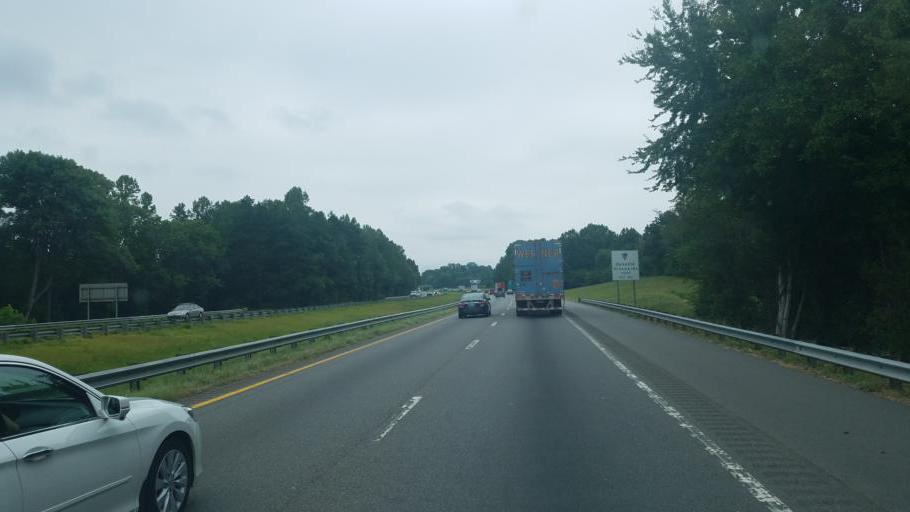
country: US
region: North Carolina
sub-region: Iredell County
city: Troutman
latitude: 35.6544
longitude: -80.8621
